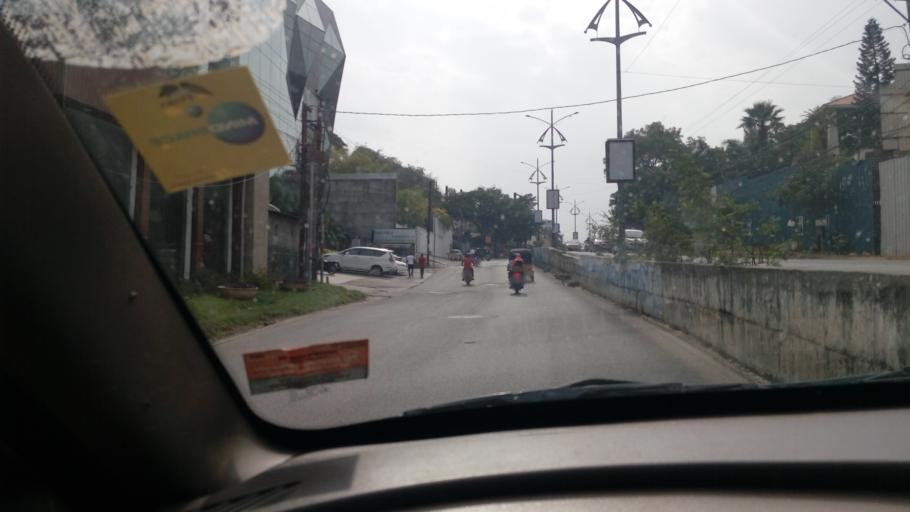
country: IN
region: Telangana
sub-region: Rangareddi
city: Kukatpalli
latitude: 17.4349
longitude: 78.4097
